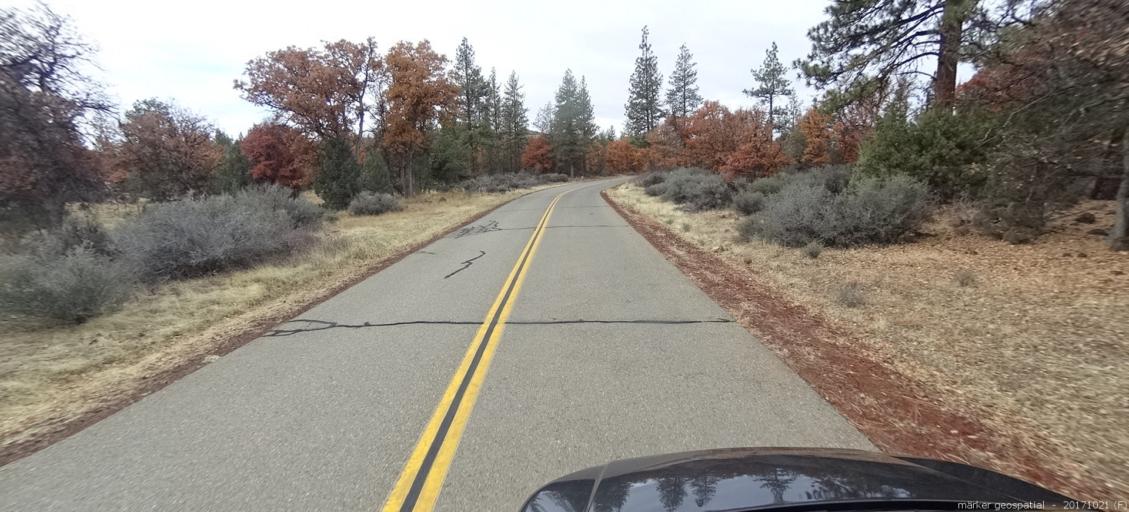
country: US
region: California
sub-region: Shasta County
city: Burney
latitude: 40.9316
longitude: -121.5558
